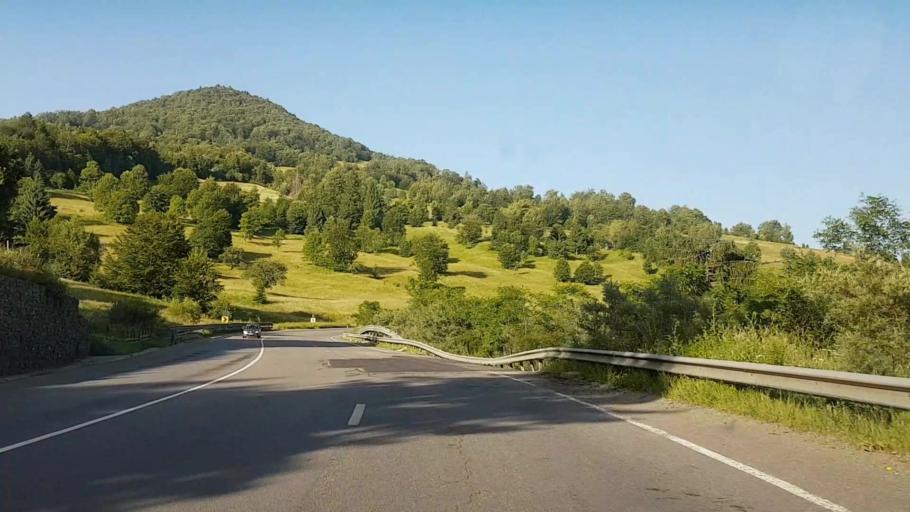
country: RO
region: Bistrita-Nasaud
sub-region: Comuna Tiha Bargaului
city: Tureac
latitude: 47.2231
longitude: 24.9255
